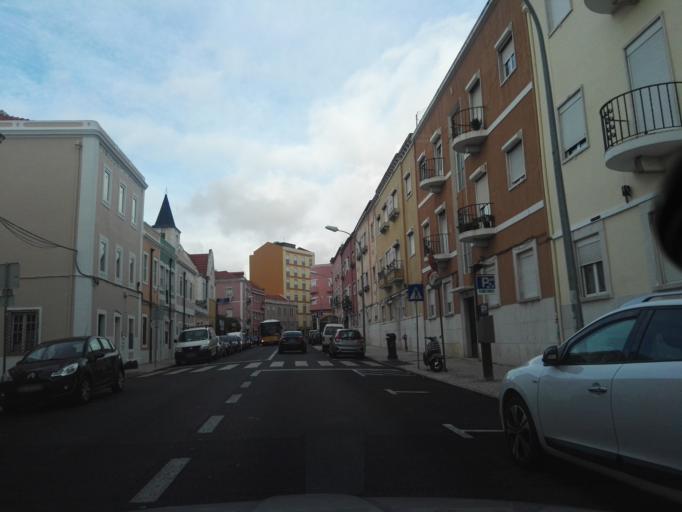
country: PT
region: Lisbon
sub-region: Lisbon
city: Lisbon
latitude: 38.7183
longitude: -9.1715
